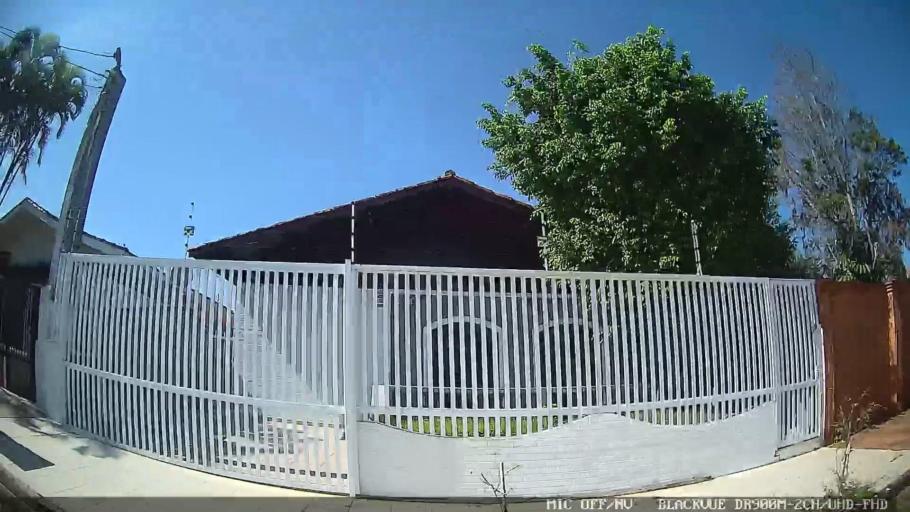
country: BR
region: Sao Paulo
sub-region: Peruibe
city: Peruibe
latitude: -24.2948
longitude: -46.9655
